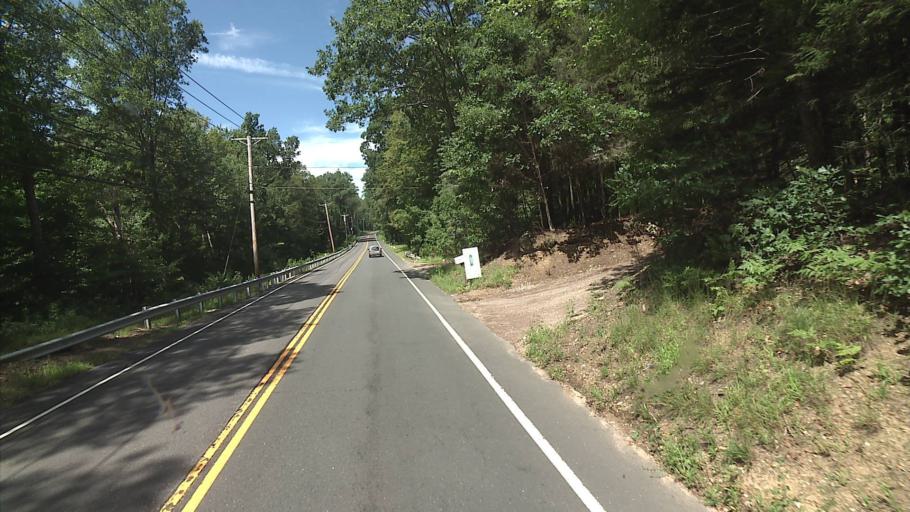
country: US
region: Connecticut
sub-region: Tolland County
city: Tolland
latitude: 41.8458
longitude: -72.3250
